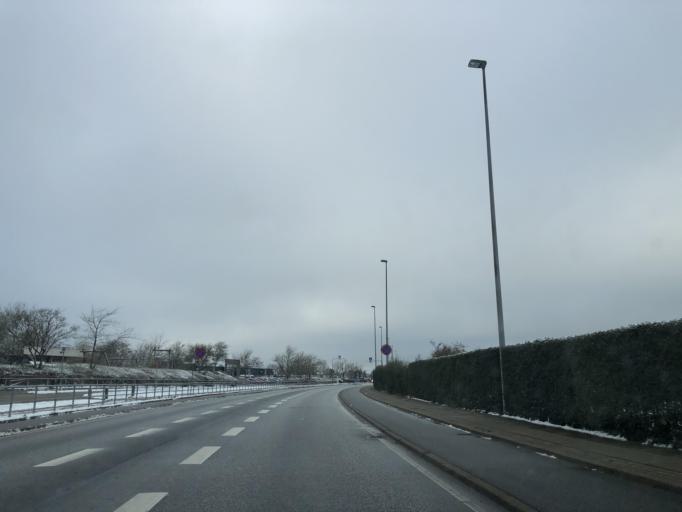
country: DK
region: Central Jutland
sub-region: Horsens Kommune
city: Horsens
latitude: 55.8355
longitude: 9.8362
